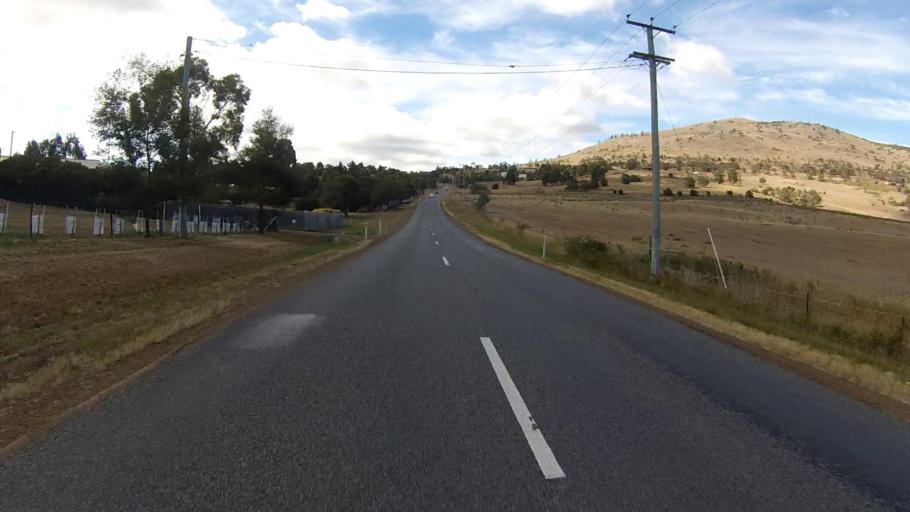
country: AU
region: Tasmania
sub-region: Glenorchy
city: Austins Ferry
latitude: -42.7225
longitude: 147.2814
